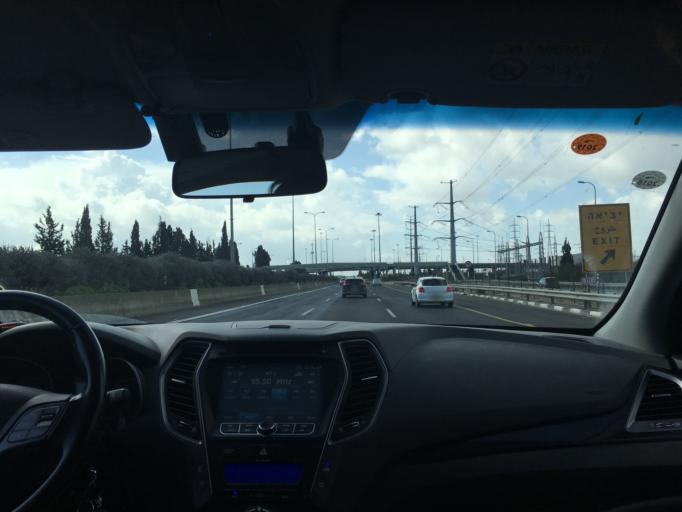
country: IL
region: Tel Aviv
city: Azor
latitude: 32.0238
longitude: 34.8250
